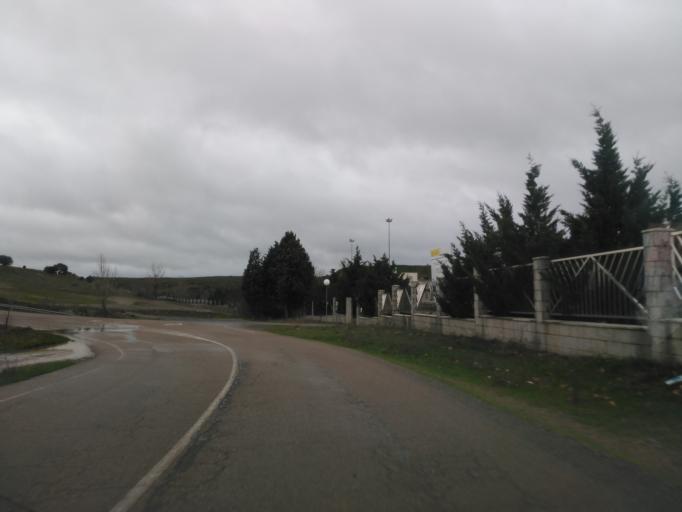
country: ES
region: Castille and Leon
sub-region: Provincia de Salamanca
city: Doninos de Salamanca
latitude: 40.9714
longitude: -5.7141
